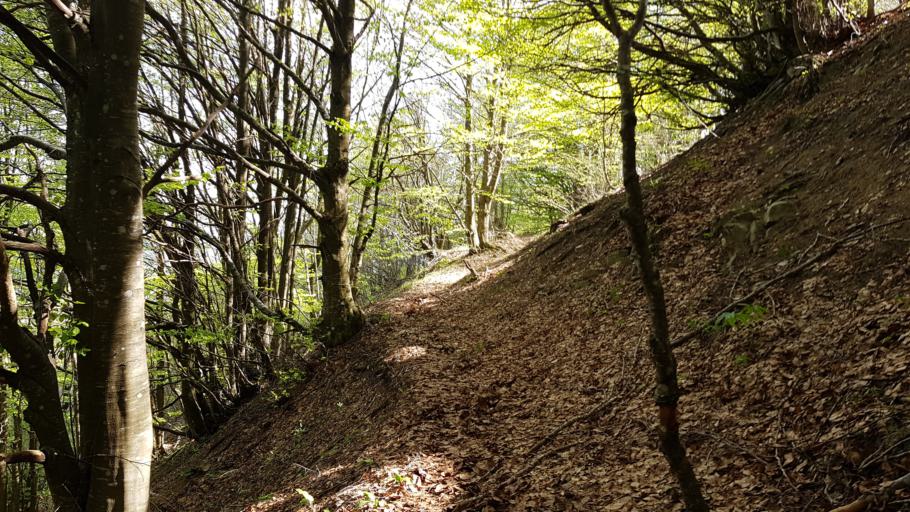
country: IT
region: Piedmont
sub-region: Provincia di Alessandria
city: Carrega Ligure
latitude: 44.6142
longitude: 9.2058
